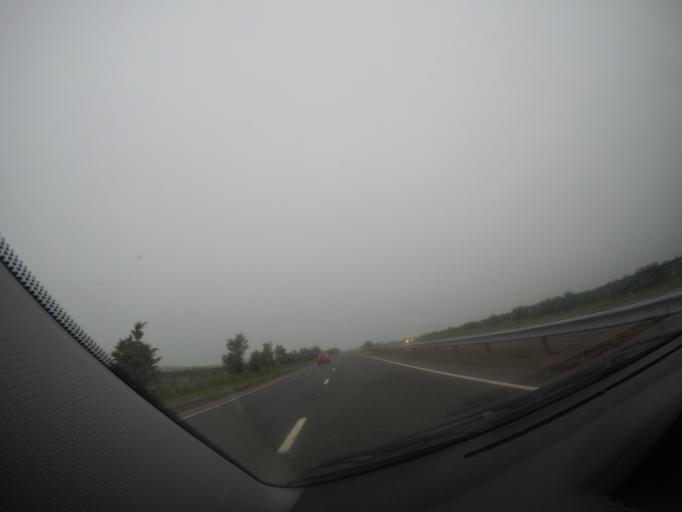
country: GB
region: Scotland
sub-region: Angus
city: Forfar
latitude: 56.5626
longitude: -2.9216
